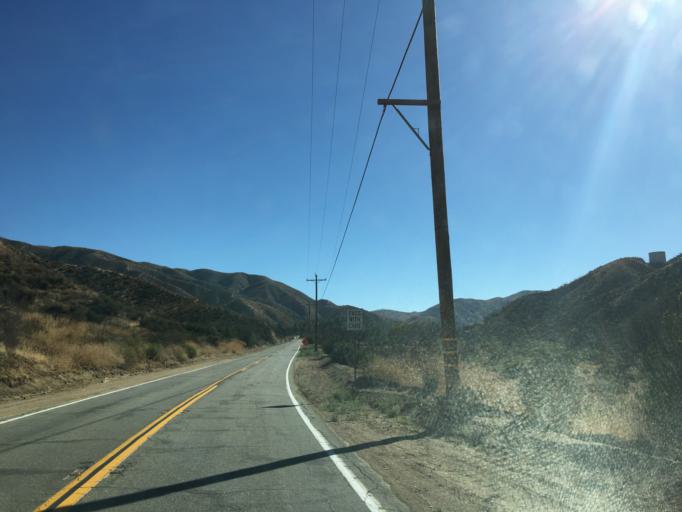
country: US
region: California
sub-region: Los Angeles County
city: Green Valley
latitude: 34.6495
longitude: -118.4859
